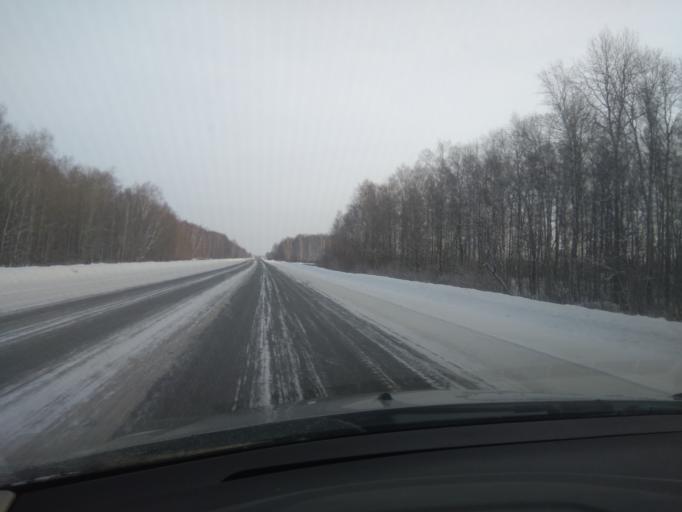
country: RU
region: Sverdlovsk
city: Bogdanovich
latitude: 56.8029
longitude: 62.0232
